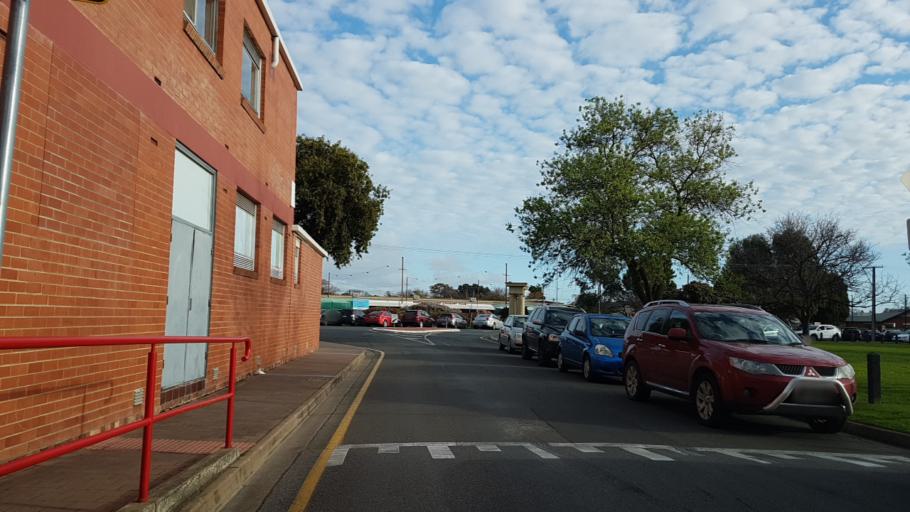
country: AU
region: South Australia
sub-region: Prospect
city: Prospect
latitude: -34.8855
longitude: 138.5999
